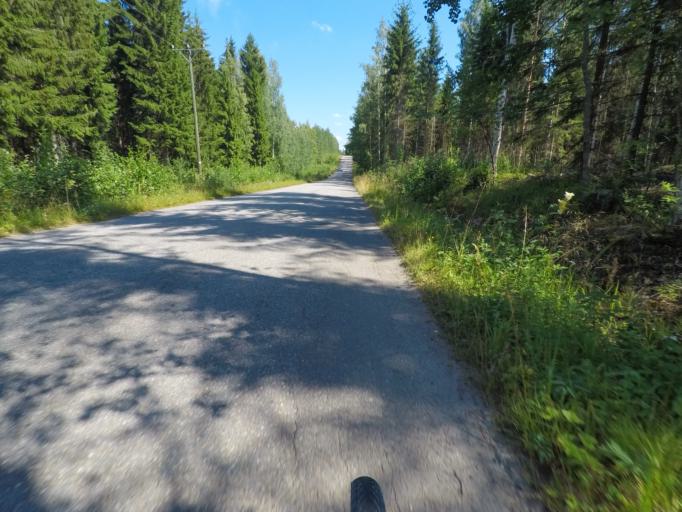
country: FI
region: Southern Savonia
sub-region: Mikkeli
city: Puumala
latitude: 61.4224
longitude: 28.1358
